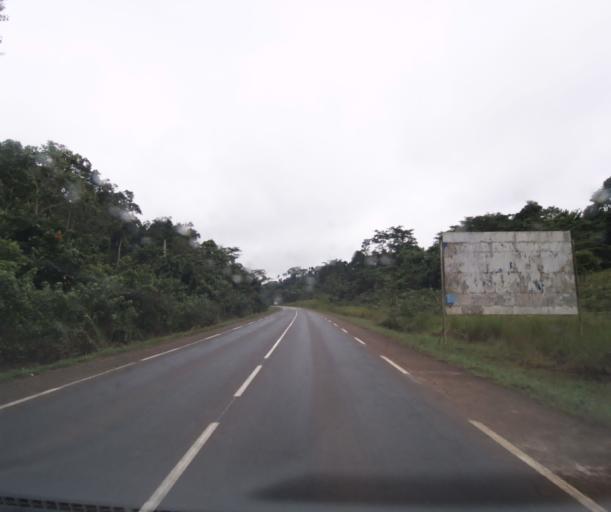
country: CM
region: Centre
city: Mbankomo
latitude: 3.7668
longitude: 11.1877
